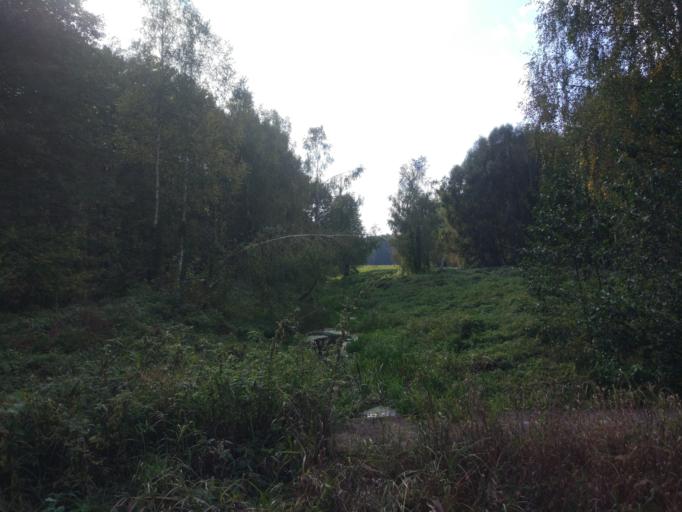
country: RU
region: Brjansk
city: Vyshkov
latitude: 52.5580
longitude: 31.6224
